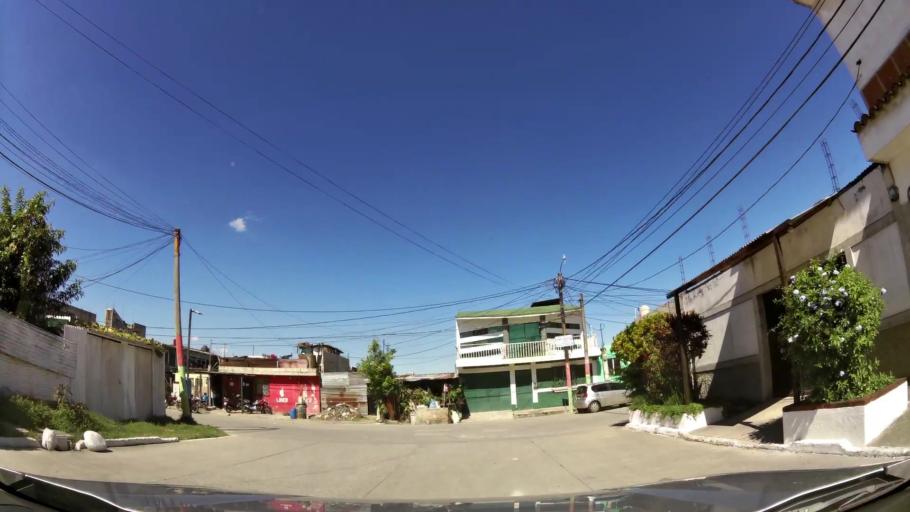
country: GT
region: Guatemala
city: Petapa
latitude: 14.5065
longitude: -90.5640
